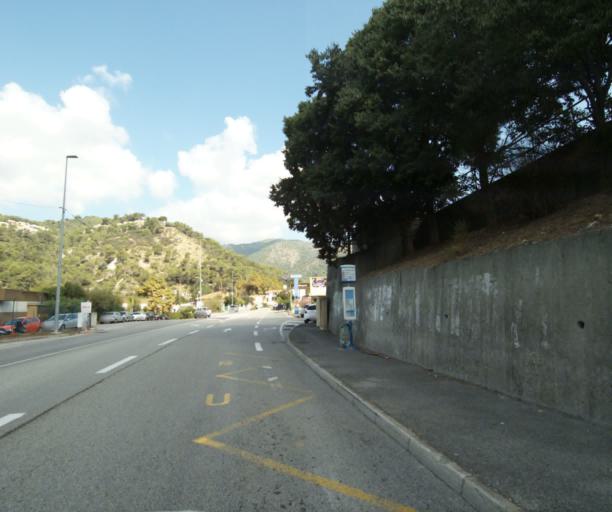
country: FR
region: Provence-Alpes-Cote d'Azur
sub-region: Departement des Alpes-Maritimes
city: Drap
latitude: 43.7488
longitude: 7.3206
